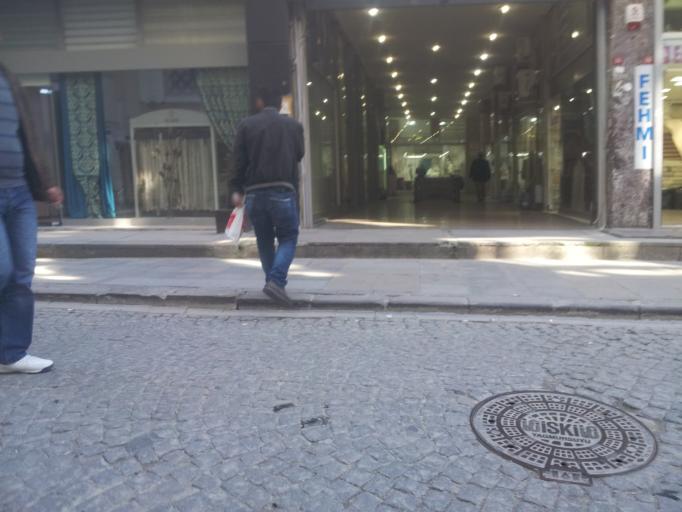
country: TR
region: Istanbul
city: Eminoenue
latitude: 41.0148
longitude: 28.9723
